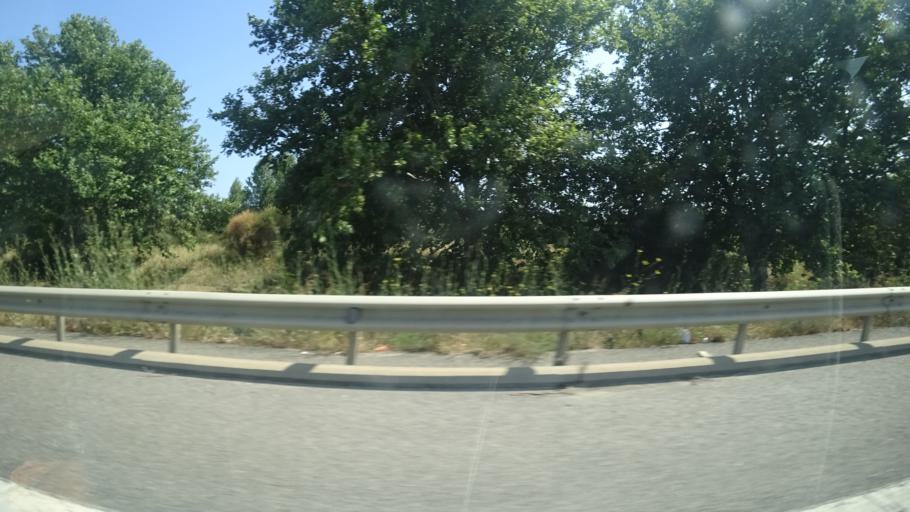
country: FR
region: Languedoc-Roussillon
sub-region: Departement des Pyrenees-Orientales
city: Pezilla-la-Riviere
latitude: 42.6825
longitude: 2.7543
